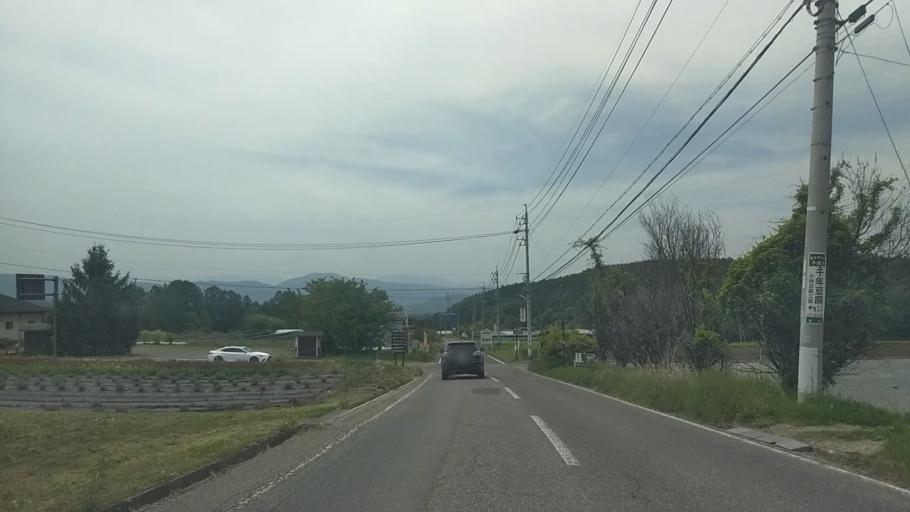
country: JP
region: Nagano
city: Chino
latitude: 36.0349
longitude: 138.2581
